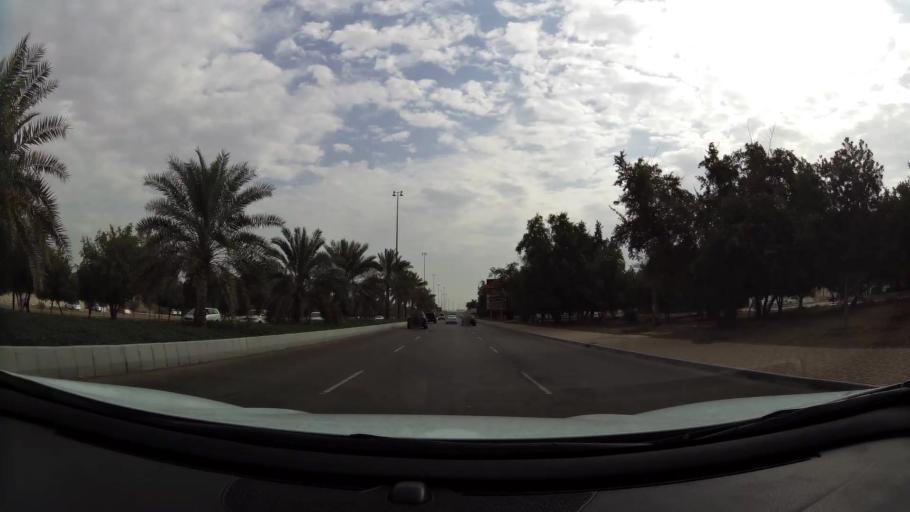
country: AE
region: Abu Dhabi
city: Al Ain
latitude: 24.2210
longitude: 55.7160
